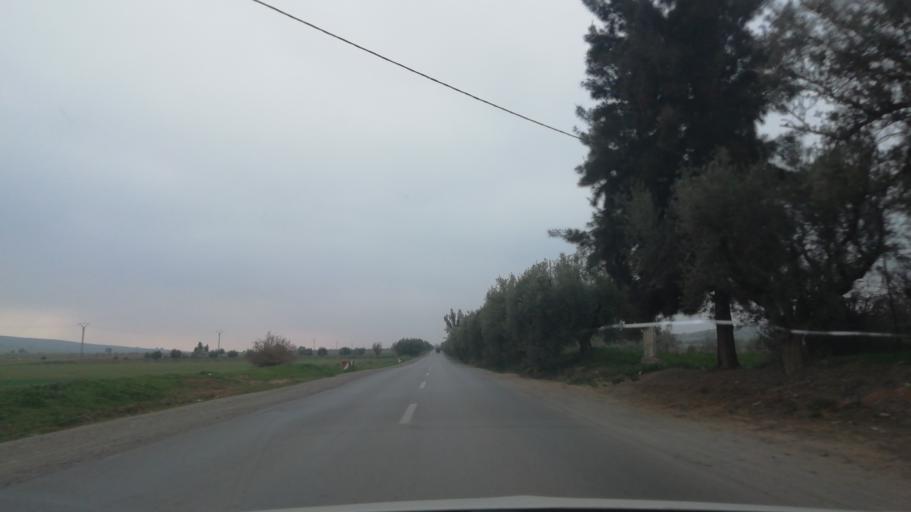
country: DZ
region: Sidi Bel Abbes
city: Sfizef
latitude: 35.2625
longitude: -0.1728
